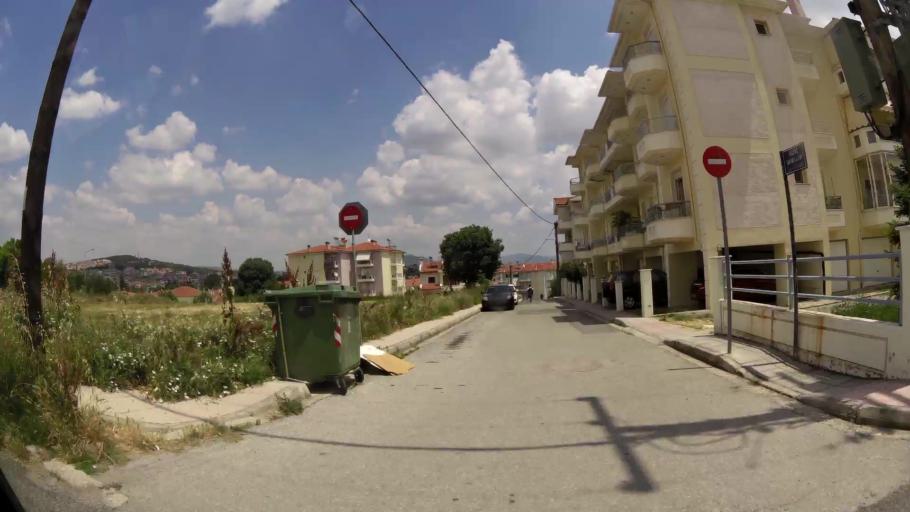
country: GR
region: West Macedonia
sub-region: Nomos Kozanis
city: Kozani
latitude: 40.2908
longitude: 21.7891
